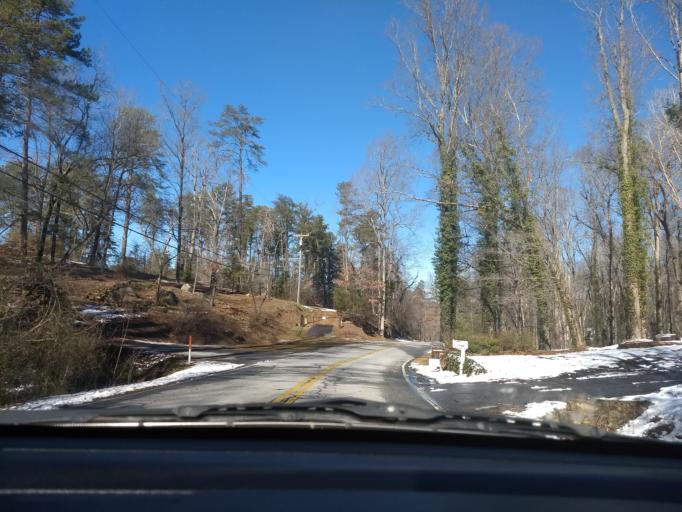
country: US
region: South Carolina
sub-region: Greenville County
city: Wade Hampton
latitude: 34.9177
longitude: -82.3691
